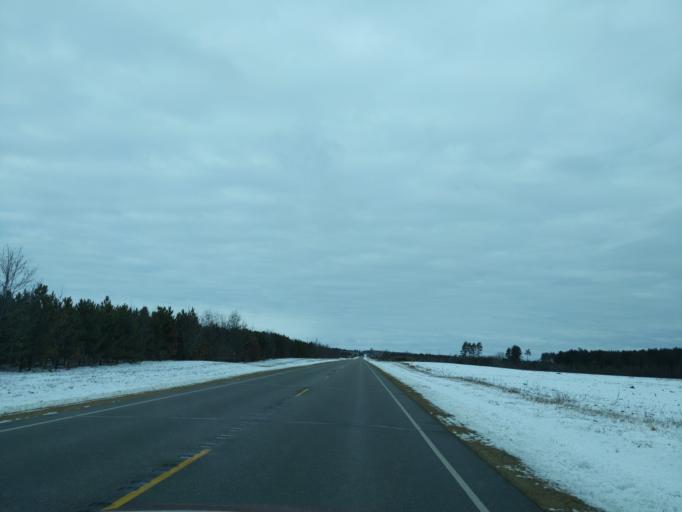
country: US
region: Wisconsin
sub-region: Waushara County
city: Wautoma
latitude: 43.9773
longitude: -89.3276
